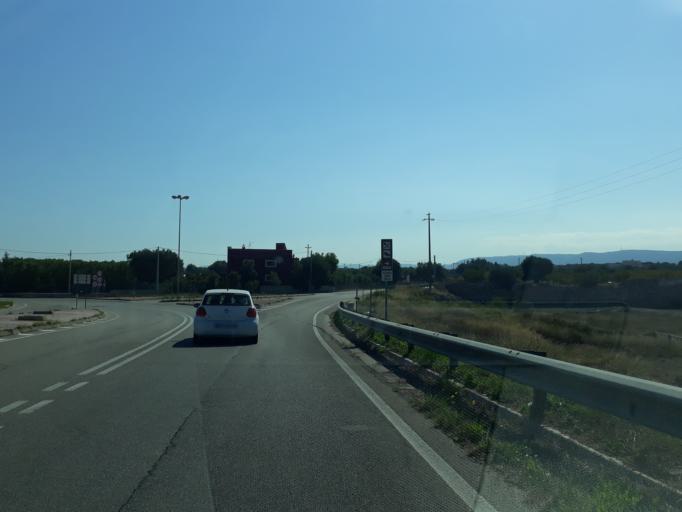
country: IT
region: Apulia
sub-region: Provincia di Bari
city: Monopoli
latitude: 40.9197
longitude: 17.3158
